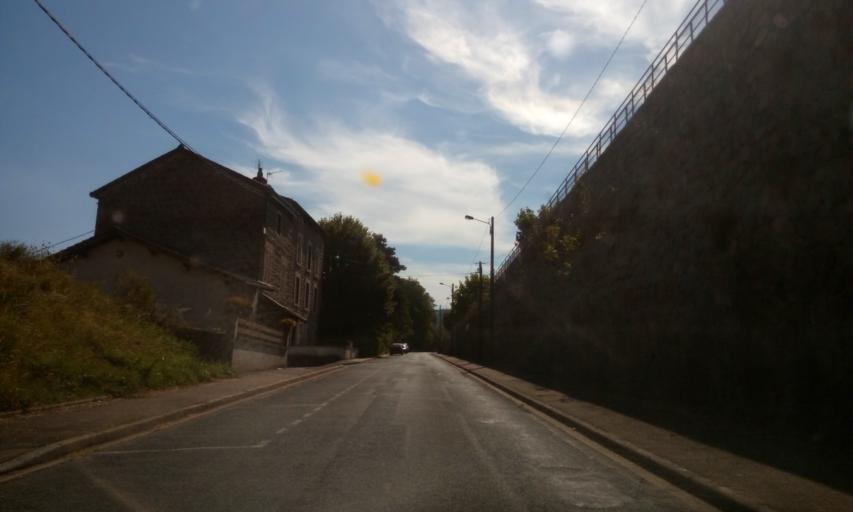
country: FR
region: Rhone-Alpes
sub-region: Departement du Rhone
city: Amplepuis
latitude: 45.9723
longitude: 4.3250
